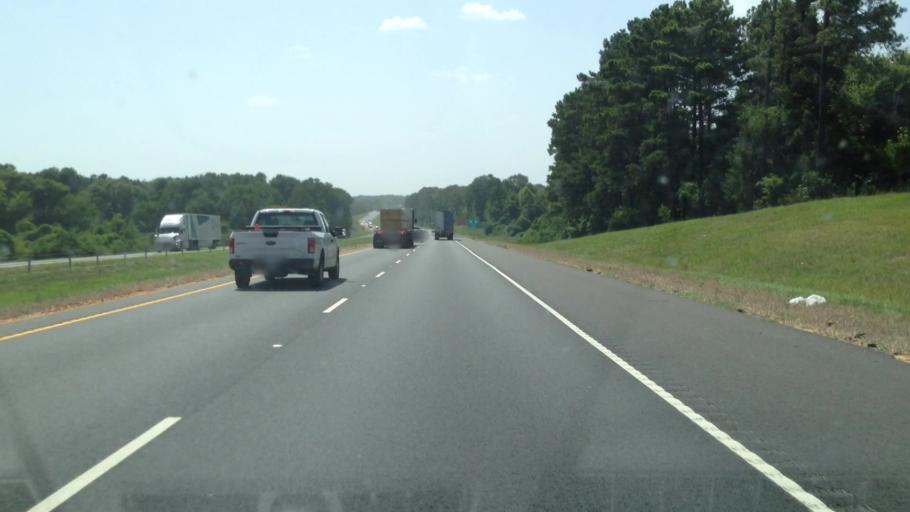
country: US
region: Louisiana
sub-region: Webster Parish
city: Minden
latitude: 32.5863
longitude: -93.2754
